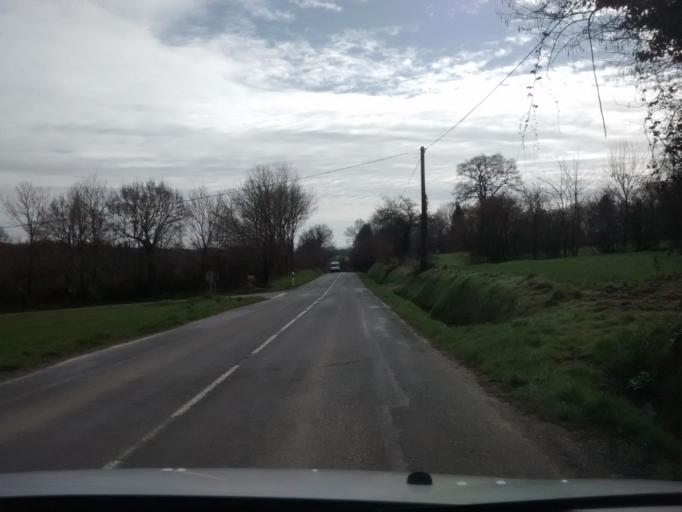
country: FR
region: Brittany
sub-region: Departement d'Ille-et-Vilaine
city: Liffre
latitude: 48.1993
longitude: -1.4776
